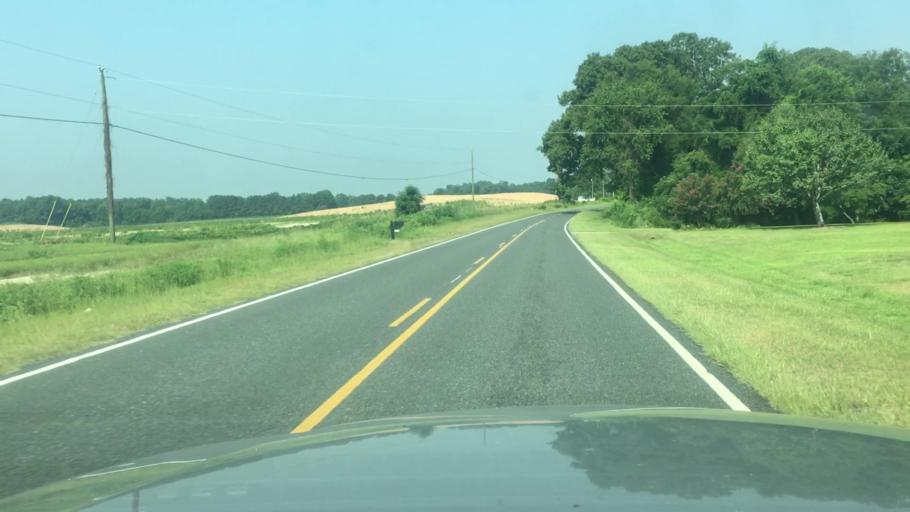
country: US
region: North Carolina
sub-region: Cumberland County
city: Hope Mills
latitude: 34.9092
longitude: -78.8609
